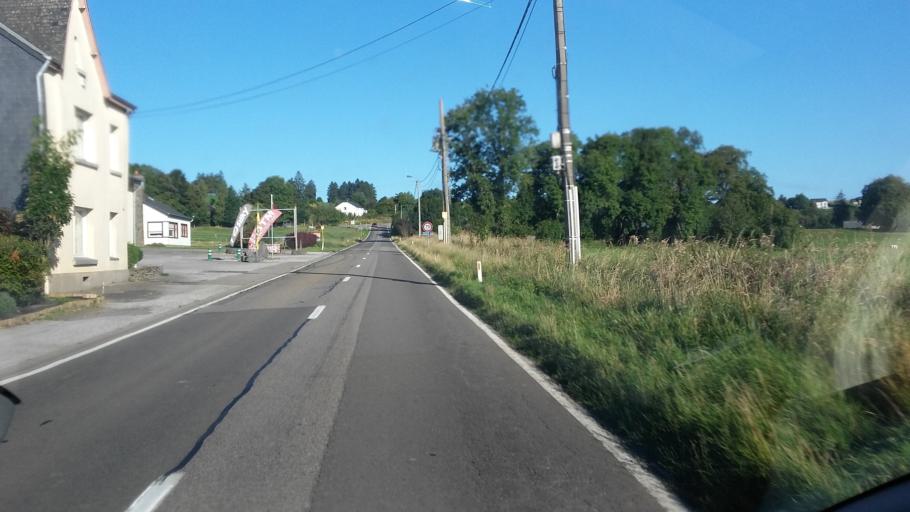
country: BE
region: Wallonia
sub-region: Province du Luxembourg
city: Neufchateau
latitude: 49.8294
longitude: 5.4825
